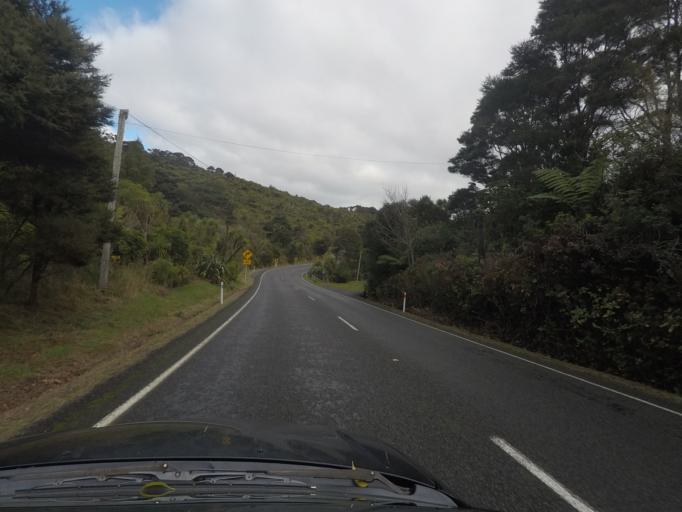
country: NZ
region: Auckland
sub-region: Auckland
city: Muriwai Beach
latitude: -36.8761
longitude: 174.5278
